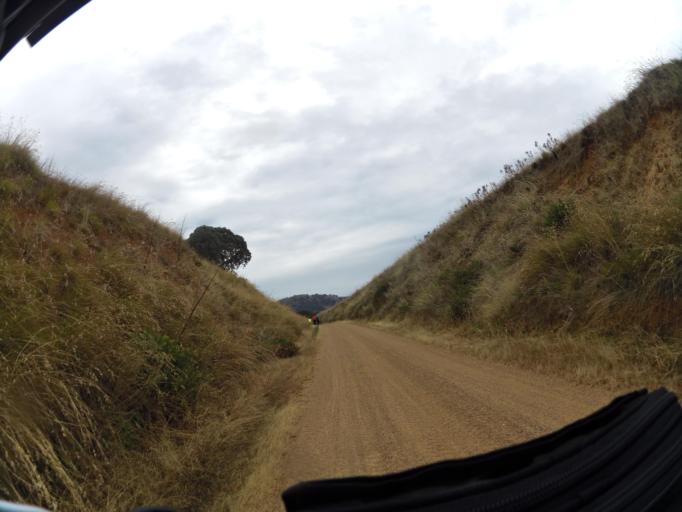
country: AU
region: New South Wales
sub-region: Albury Municipality
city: East Albury
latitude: -36.2035
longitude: 147.0503
